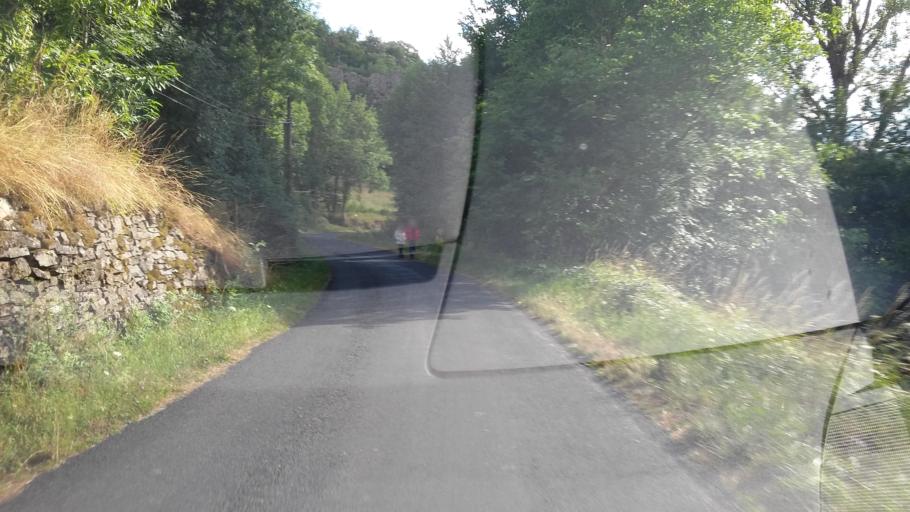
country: FR
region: Languedoc-Roussillon
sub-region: Departement de la Lozere
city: Meyrueis
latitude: 44.0252
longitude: 3.3744
